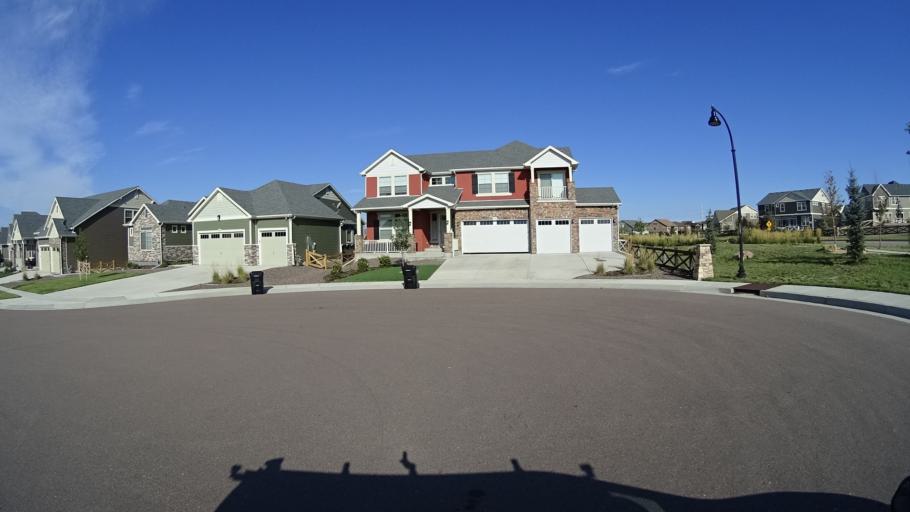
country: US
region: Colorado
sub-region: El Paso County
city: Cimarron Hills
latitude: 38.9337
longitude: -104.6703
